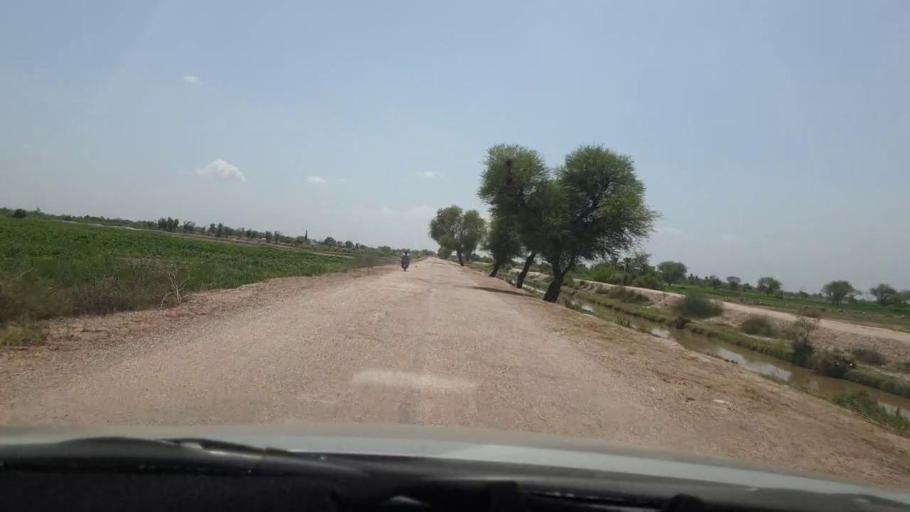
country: PK
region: Sindh
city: Pano Aqil
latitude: 27.7265
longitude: 69.1806
